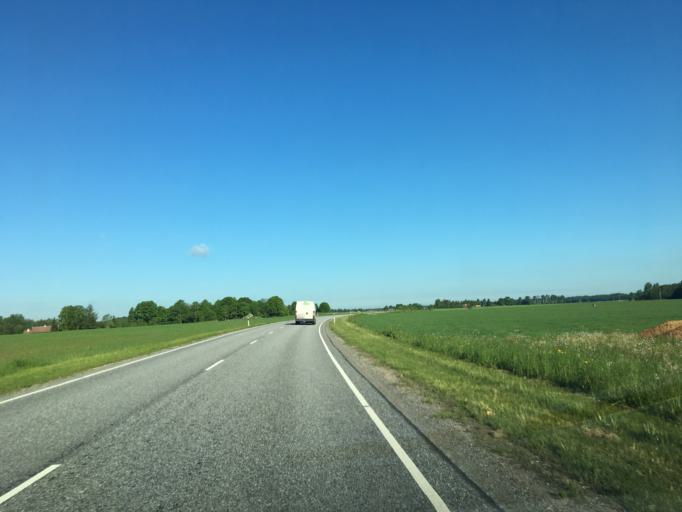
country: EE
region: Jogevamaa
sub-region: Tabivere vald
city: Tabivere
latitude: 58.4628
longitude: 26.6356
